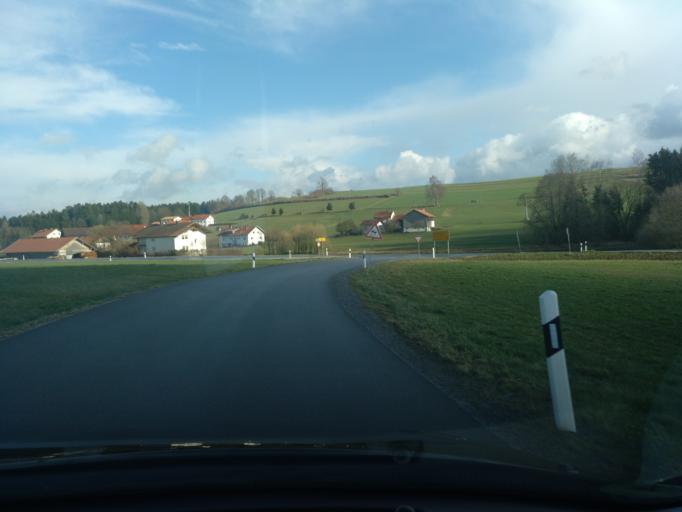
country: DE
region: Bavaria
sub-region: Upper Palatinate
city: Zandt
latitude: 49.1210
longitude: 12.7252
